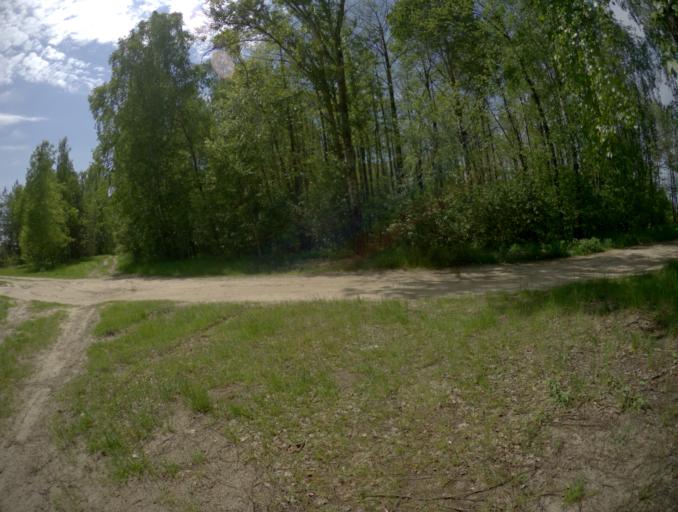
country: RU
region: Vladimir
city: Gusevskiy
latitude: 55.6826
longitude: 40.4744
